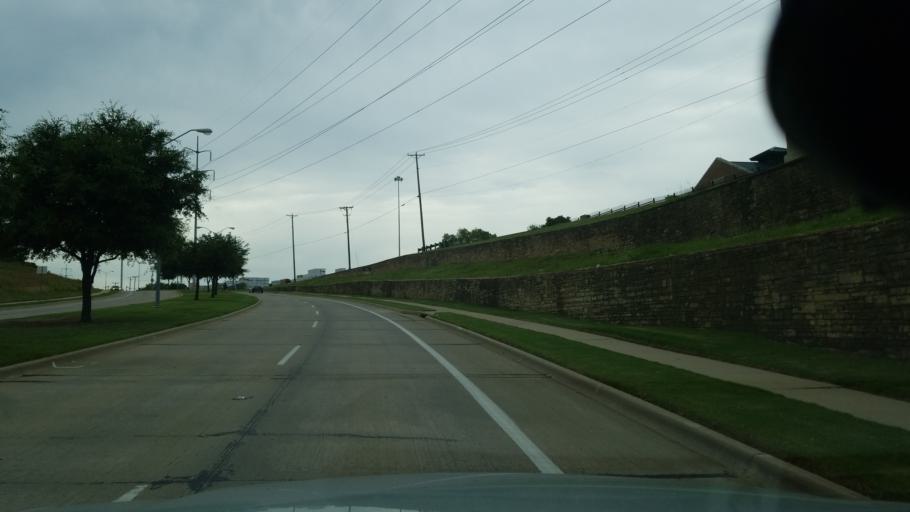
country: US
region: Texas
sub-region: Dallas County
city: Irving
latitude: 32.8446
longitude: -96.9342
